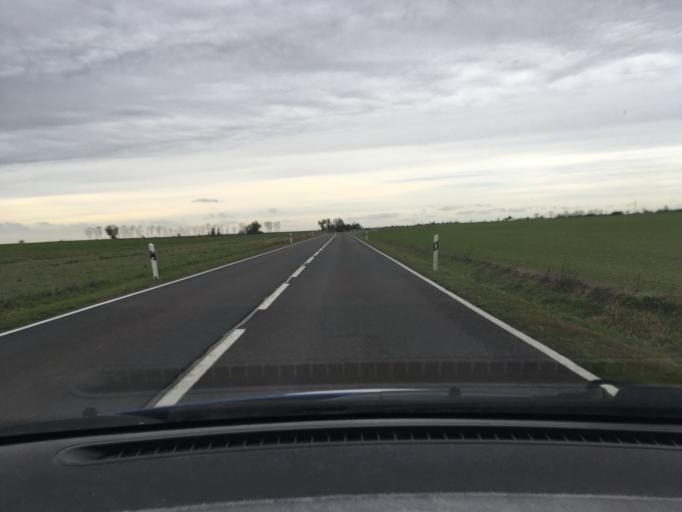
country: DE
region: Saxony-Anhalt
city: Leitzkau
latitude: 52.0385
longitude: 11.9805
